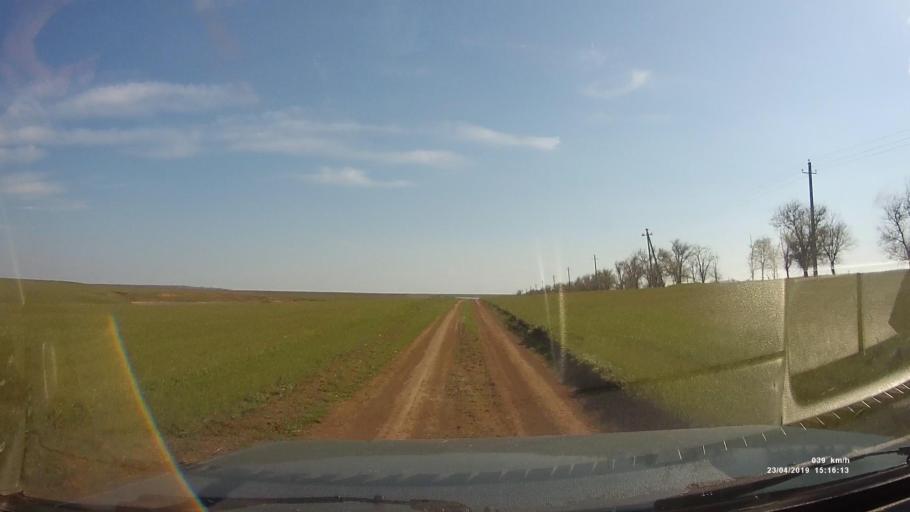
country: RU
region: Rostov
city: Remontnoye
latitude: 46.5349
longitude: 42.9698
